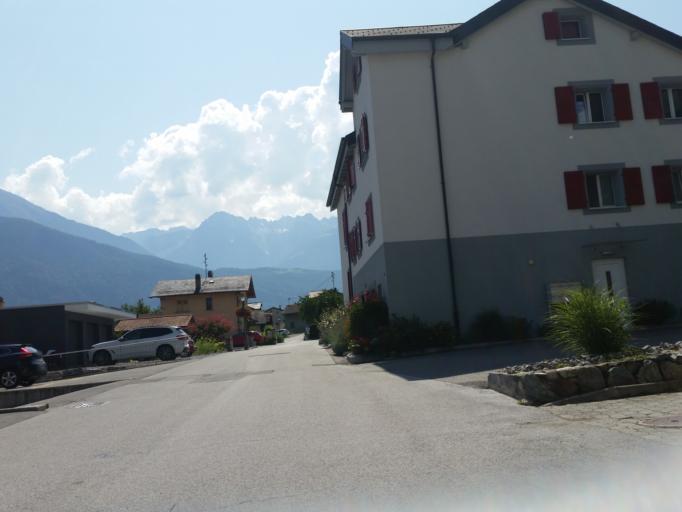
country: CH
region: Valais
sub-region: Martigny District
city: Fully
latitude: 46.1357
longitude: 7.1085
